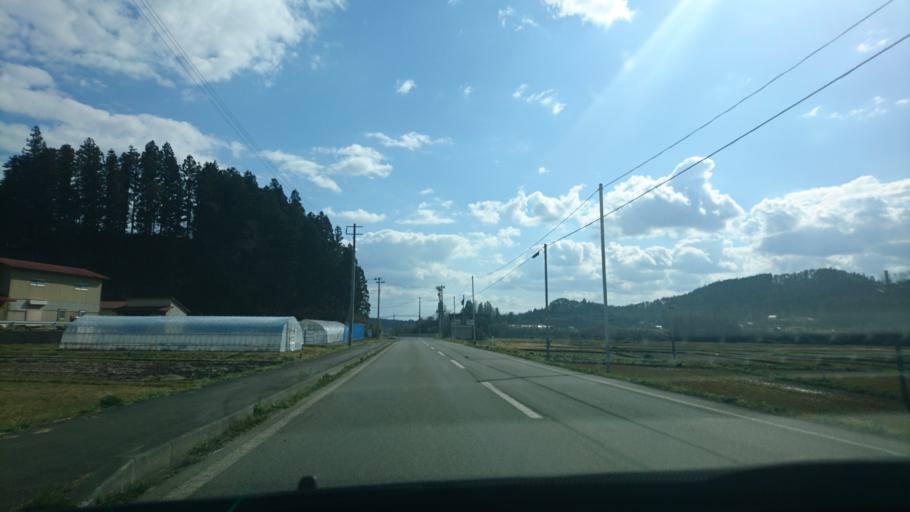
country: JP
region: Iwate
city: Kitakami
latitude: 39.2471
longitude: 141.2029
